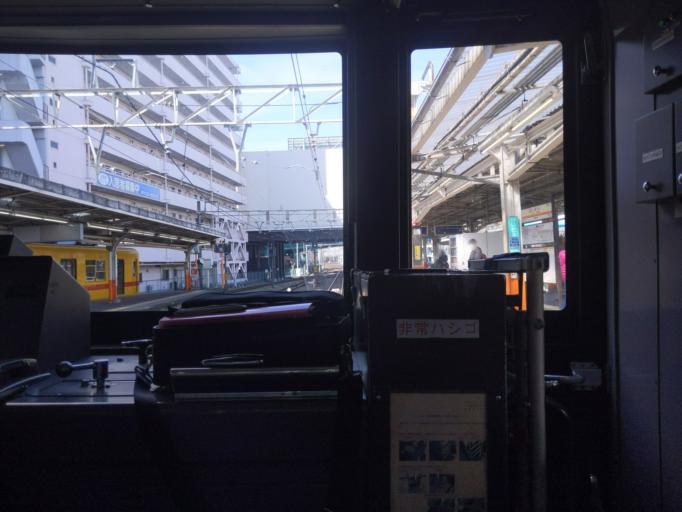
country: JP
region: Saitama
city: Soka
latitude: 35.7775
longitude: 139.7900
